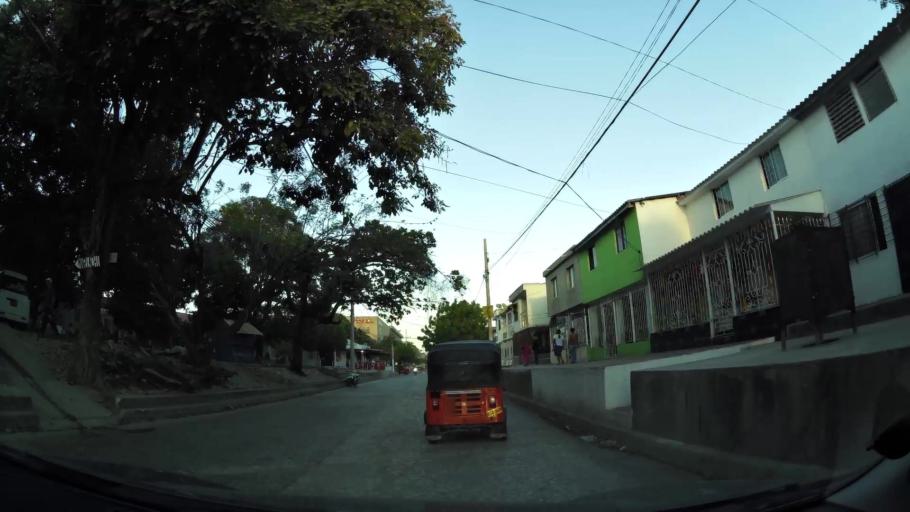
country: CO
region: Atlantico
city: Soledad
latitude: 10.9253
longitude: -74.7828
